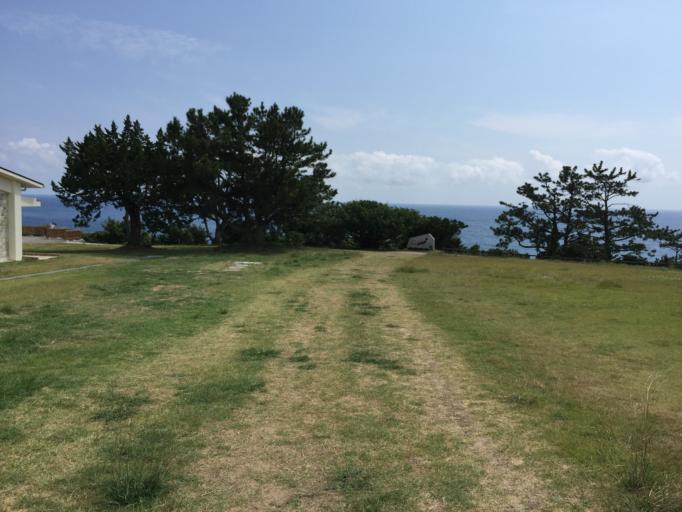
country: JP
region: Wakayama
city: Shingu
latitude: 33.4366
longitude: 135.7617
